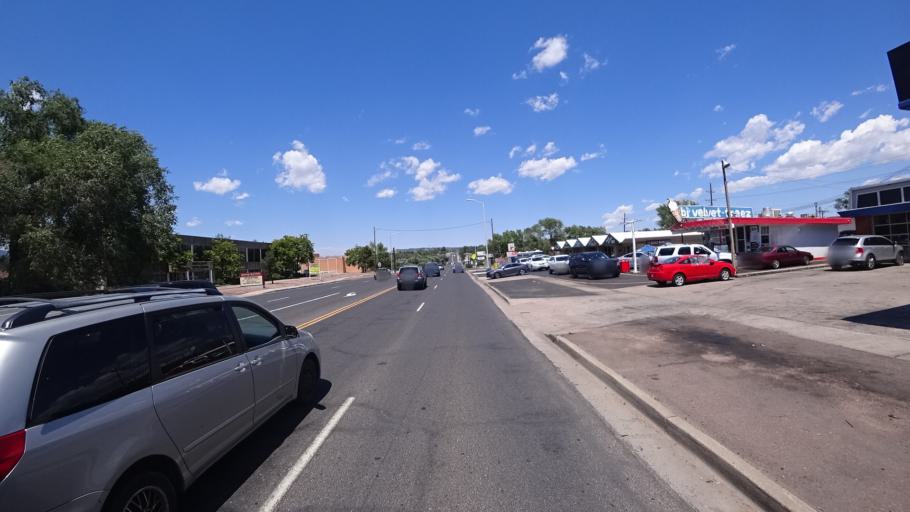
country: US
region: Colorado
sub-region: El Paso County
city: Colorado Springs
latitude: 38.8544
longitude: -104.7942
